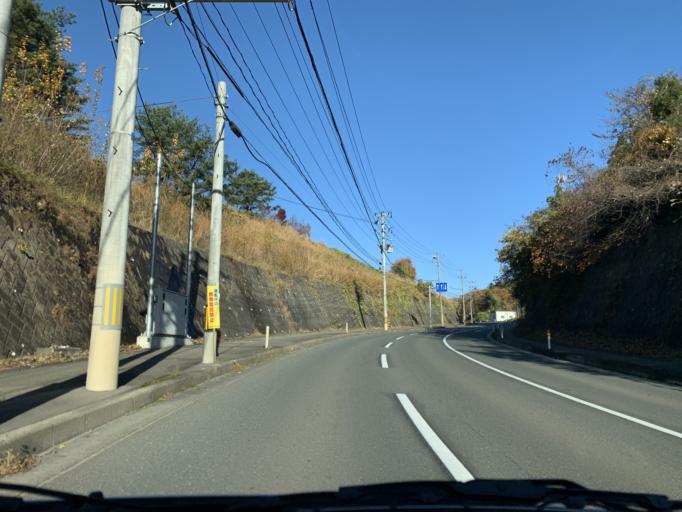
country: JP
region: Iwate
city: Mizusawa
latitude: 39.2012
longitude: 141.1731
